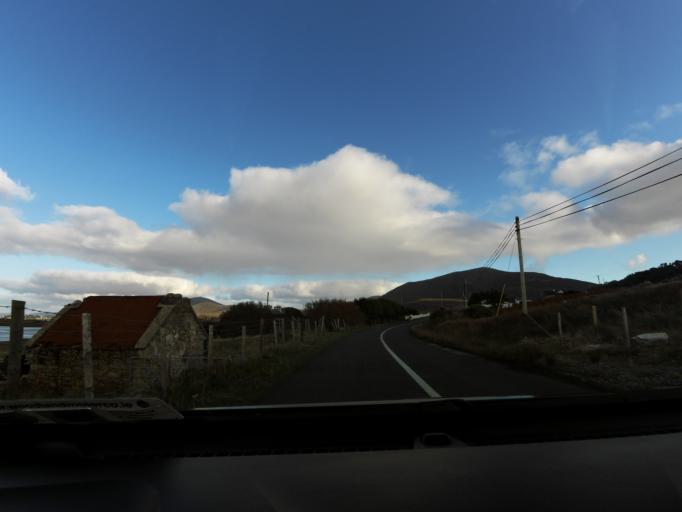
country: IE
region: Connaught
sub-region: Maigh Eo
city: Belmullet
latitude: 53.9084
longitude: -9.9490
